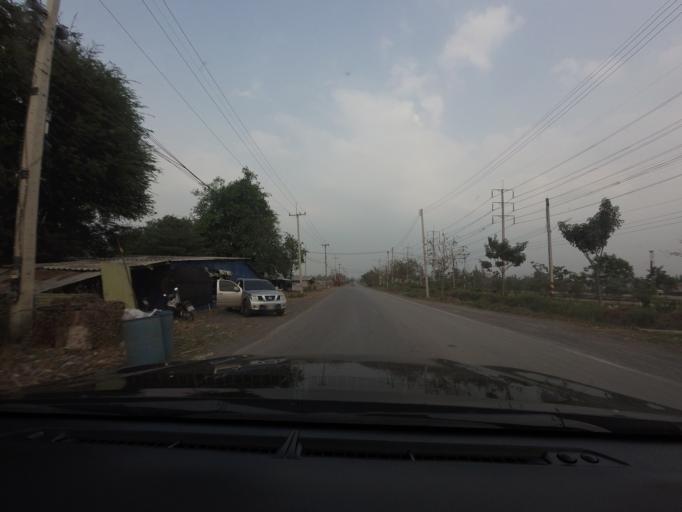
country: TH
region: Sara Buri
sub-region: Amphoe Wang Muang
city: Wang Muang
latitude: 14.8408
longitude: 101.0789
